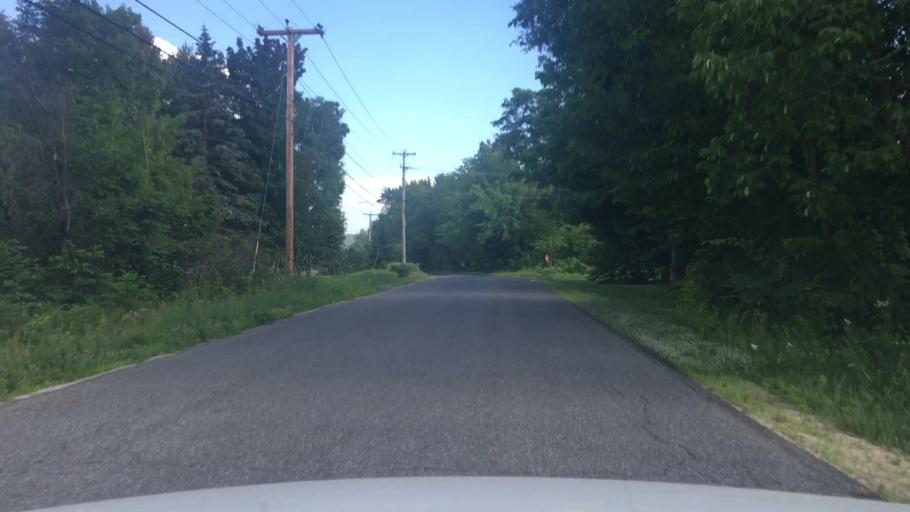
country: US
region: Maine
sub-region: Franklin County
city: Wilton
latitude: 44.6096
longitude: -70.2313
